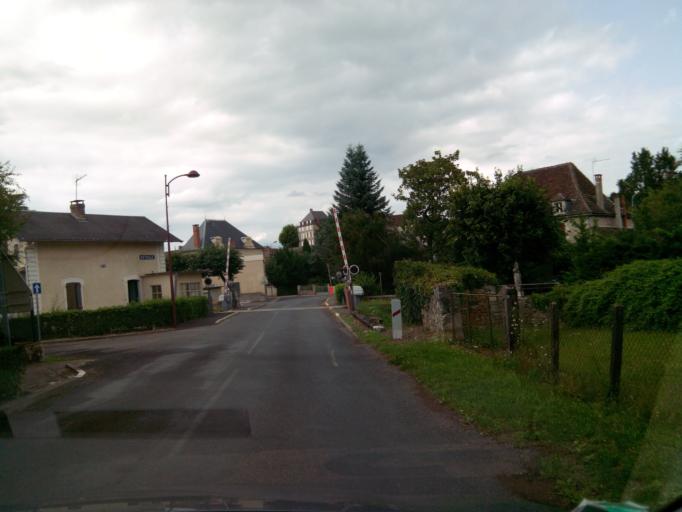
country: FR
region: Midi-Pyrenees
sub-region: Departement du Lot
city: Vayrac
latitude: 44.9420
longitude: 1.7348
